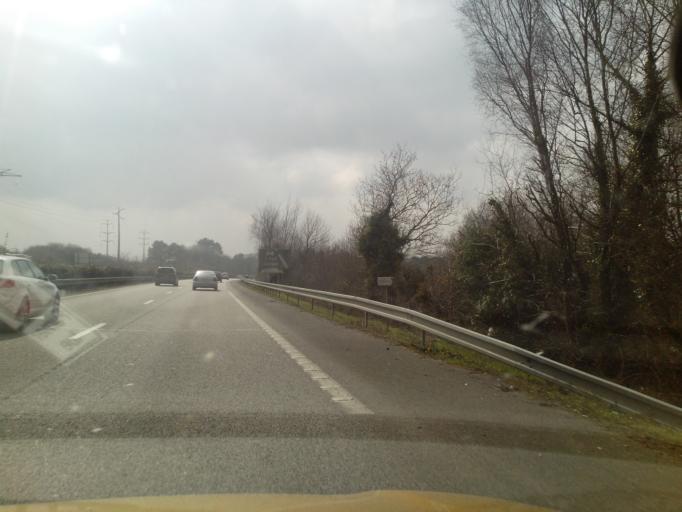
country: FR
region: Brittany
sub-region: Departement du Morbihan
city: Saint-Nolff
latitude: 47.6824
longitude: -2.6498
